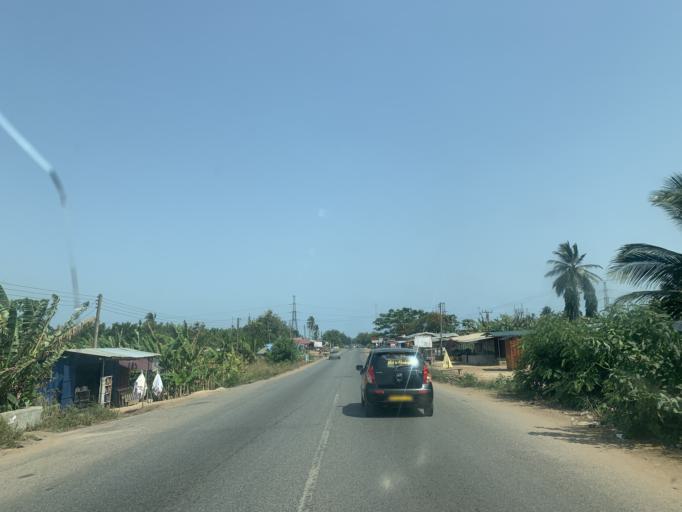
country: GH
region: Central
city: Winneba
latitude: 5.3911
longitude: -0.6463
